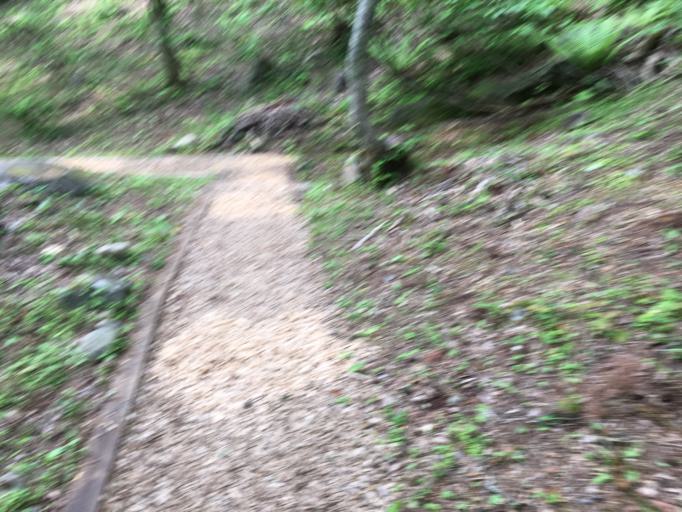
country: JP
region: Fukushima
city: Inawashiro
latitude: 37.6521
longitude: 140.0919
